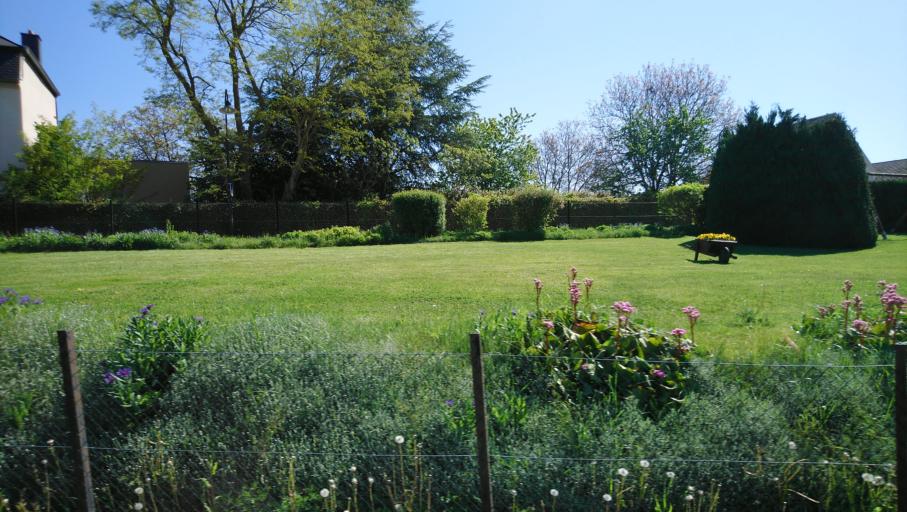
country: LU
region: Diekirch
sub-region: Canton de Vianden
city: Tandel
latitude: 49.9118
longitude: 6.1939
